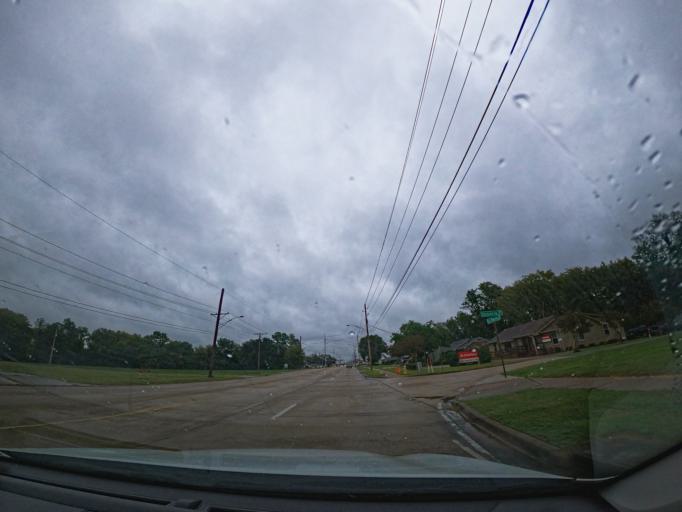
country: US
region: Louisiana
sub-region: Bossier Parish
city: Bossier City
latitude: 32.5205
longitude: -93.6992
